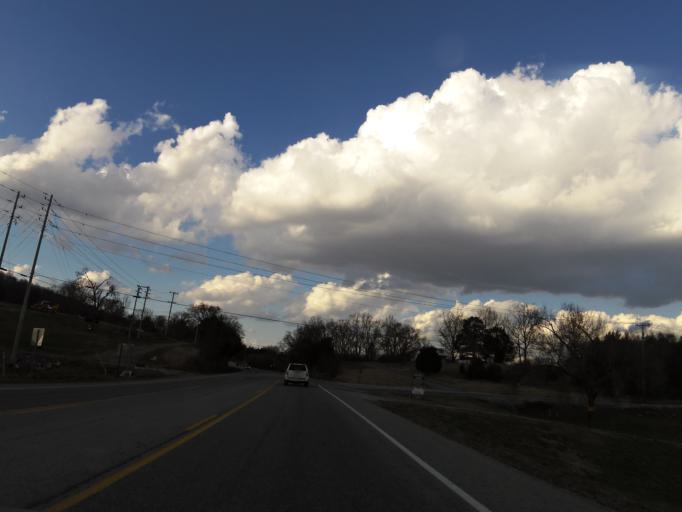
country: US
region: Tennessee
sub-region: Smith County
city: South Carthage
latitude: 36.2038
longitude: -85.9518
